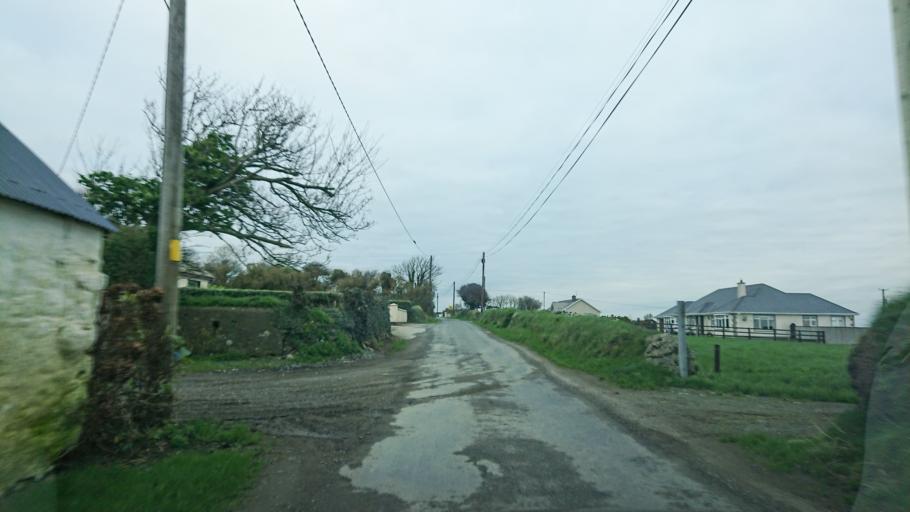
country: IE
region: Munster
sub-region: Waterford
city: Tra Mhor
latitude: 52.1418
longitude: -7.1815
